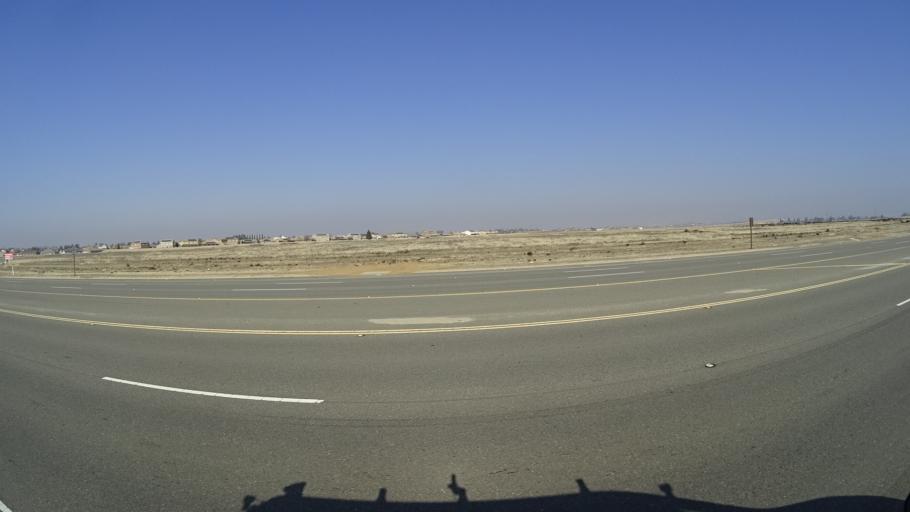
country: US
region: California
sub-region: Kern County
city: Bakersfield
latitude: 35.3980
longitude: -118.8847
